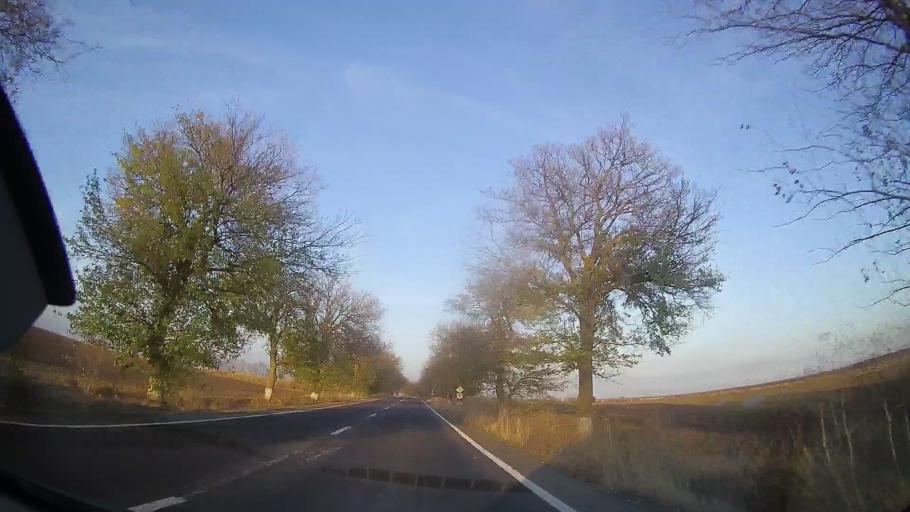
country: RO
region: Constanta
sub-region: Comuna Amzacea
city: Amzacea
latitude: 43.9535
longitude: 28.3854
